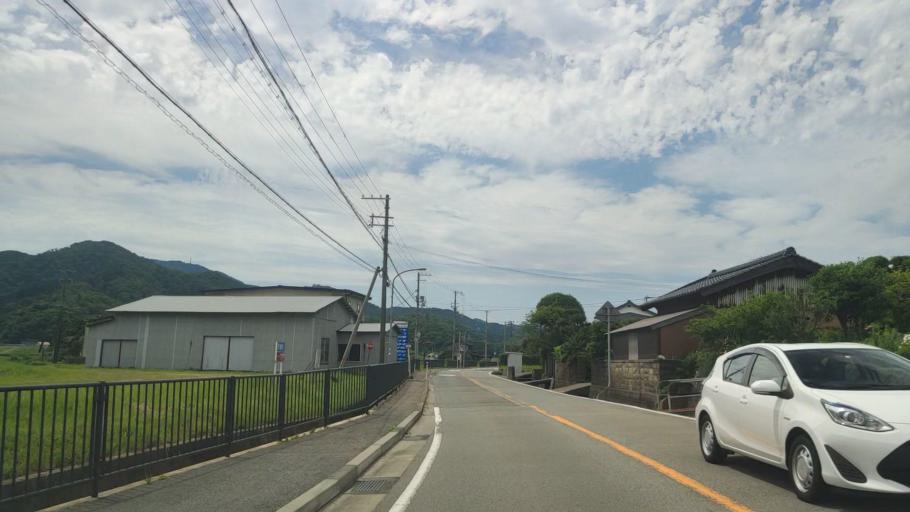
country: JP
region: Hyogo
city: Toyooka
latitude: 35.6460
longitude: 134.7580
